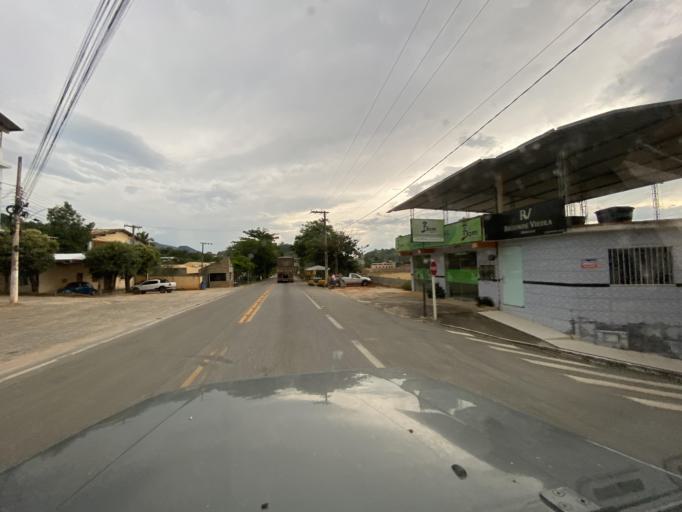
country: BR
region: Espirito Santo
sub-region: Jeronimo Monteiro
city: Jeronimo Monteiro
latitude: -20.7908
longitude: -41.3881
